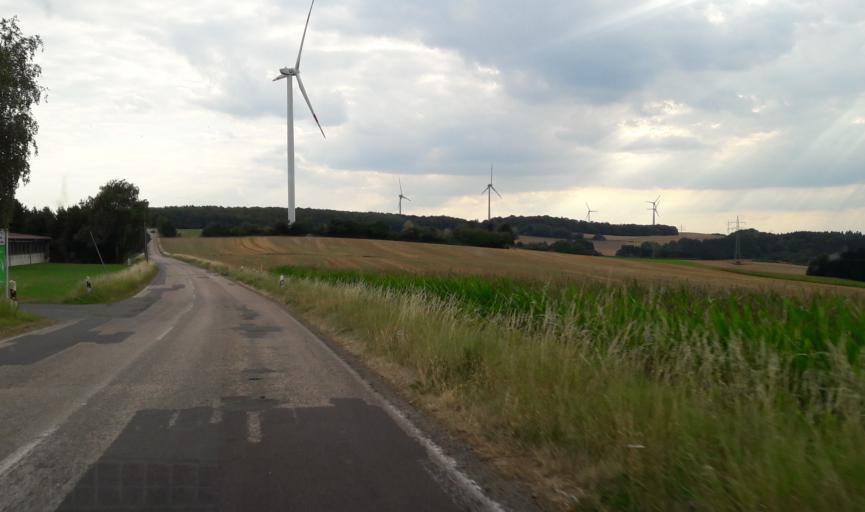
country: DE
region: Saarland
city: Tholey
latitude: 49.4441
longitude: 7.0031
